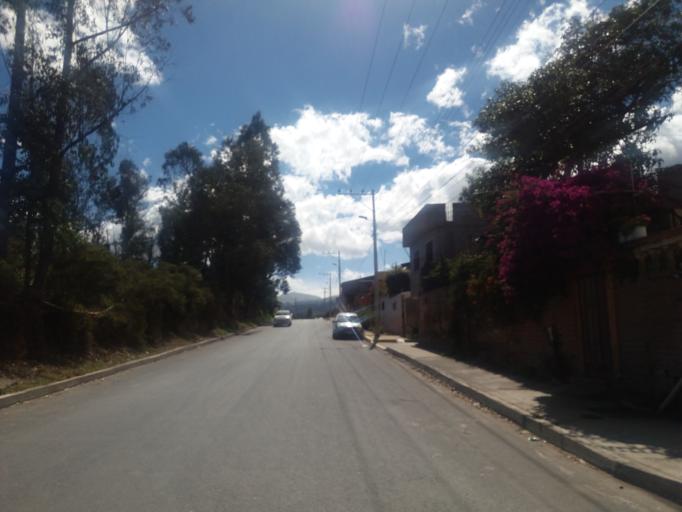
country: EC
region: Pichincha
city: Quito
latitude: -0.1694
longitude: -78.3381
